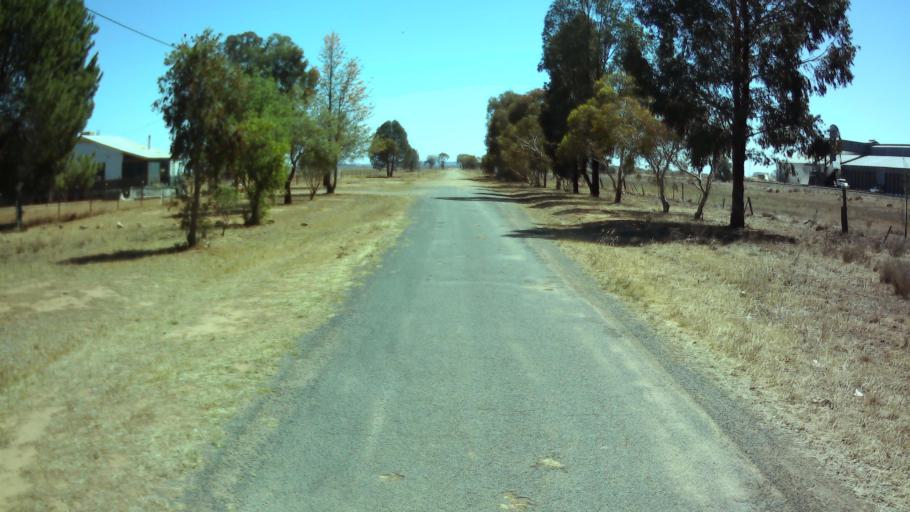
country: AU
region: New South Wales
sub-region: Weddin
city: Grenfell
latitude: -33.8398
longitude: 147.7413
